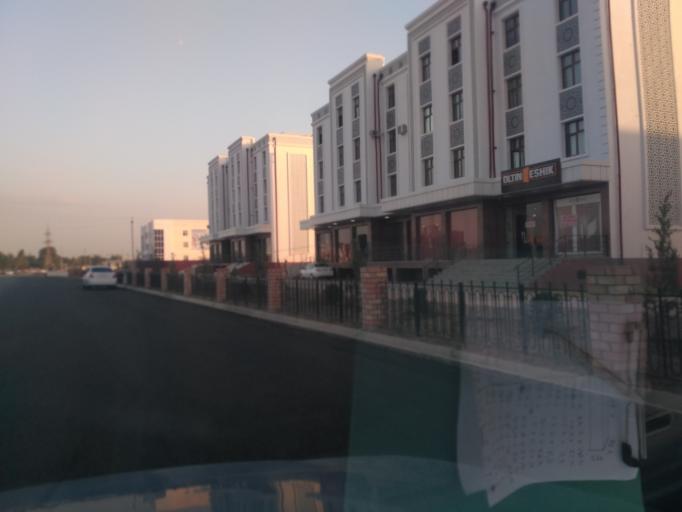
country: UZ
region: Sirdaryo
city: Guliston
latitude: 40.5068
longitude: 68.7674
